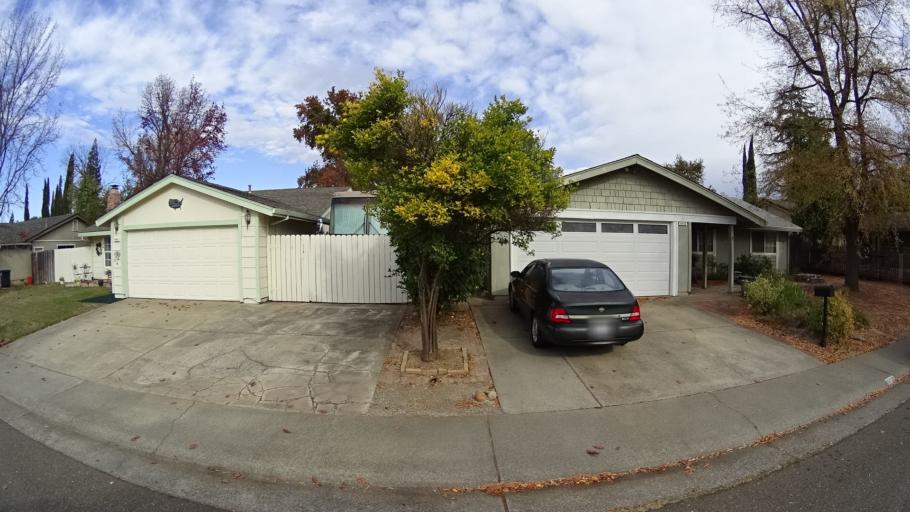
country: US
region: California
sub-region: Sacramento County
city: Citrus Heights
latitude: 38.7087
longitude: -121.2460
